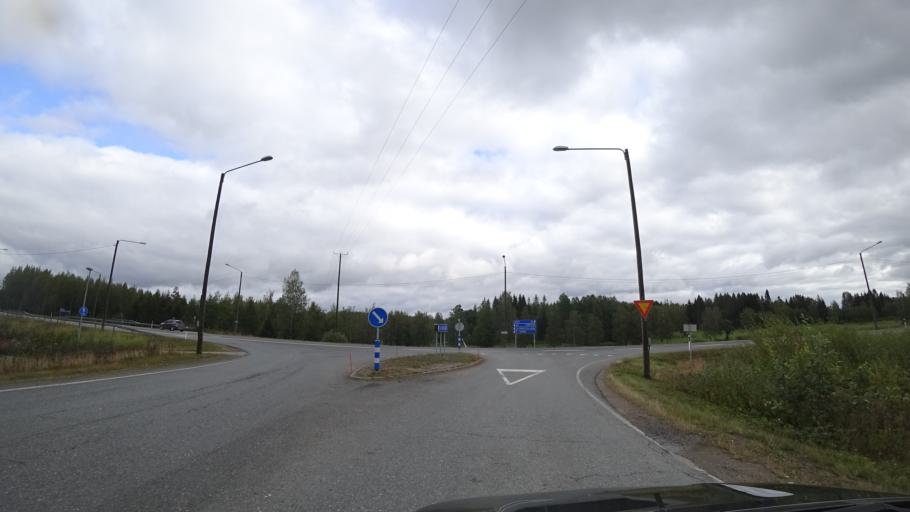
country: FI
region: Haeme
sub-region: Haemeenlinna
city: Lammi
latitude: 61.0514
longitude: 25.0086
